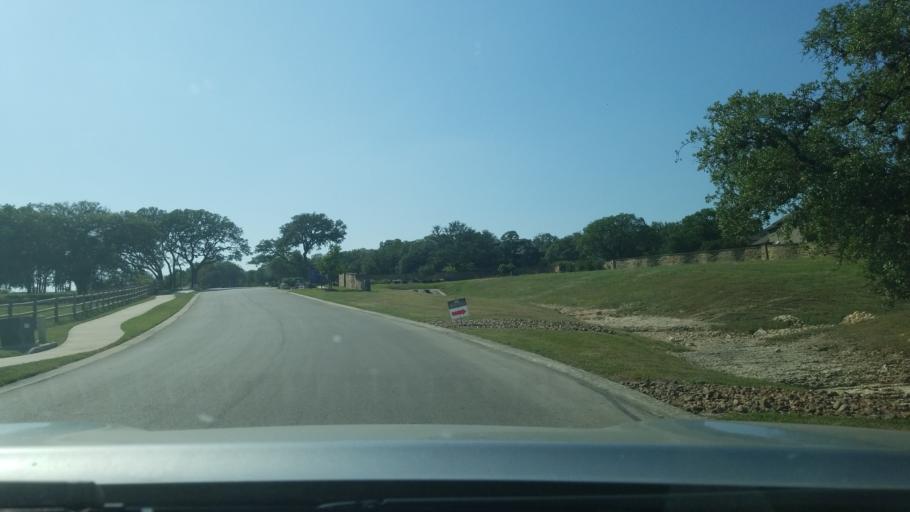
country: US
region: Texas
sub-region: Comal County
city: Bulverde
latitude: 29.7588
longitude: -98.4195
